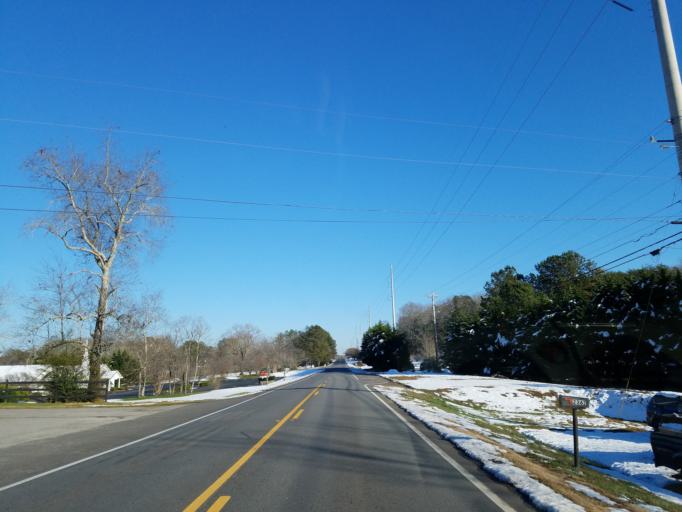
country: US
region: Georgia
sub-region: Dawson County
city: Dawsonville
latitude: 34.3537
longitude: -84.0744
